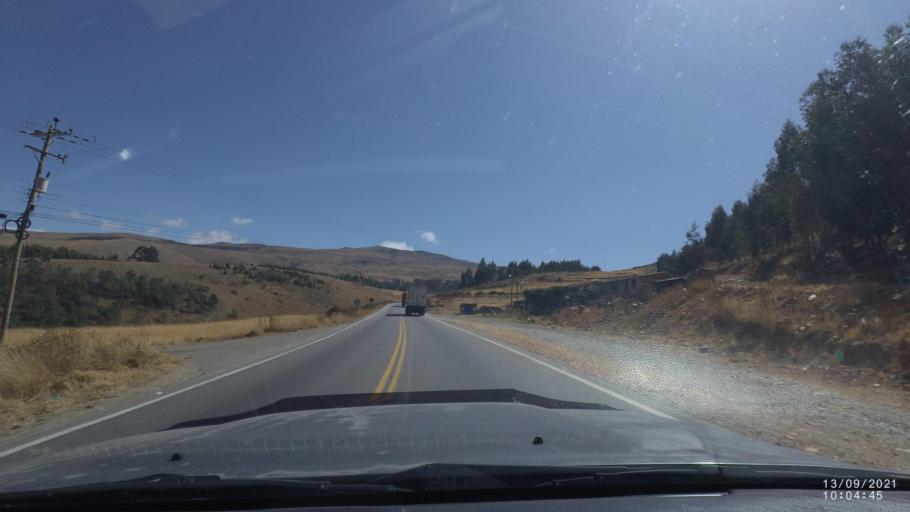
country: BO
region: Cochabamba
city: Colomi
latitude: -17.4187
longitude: -65.8981
